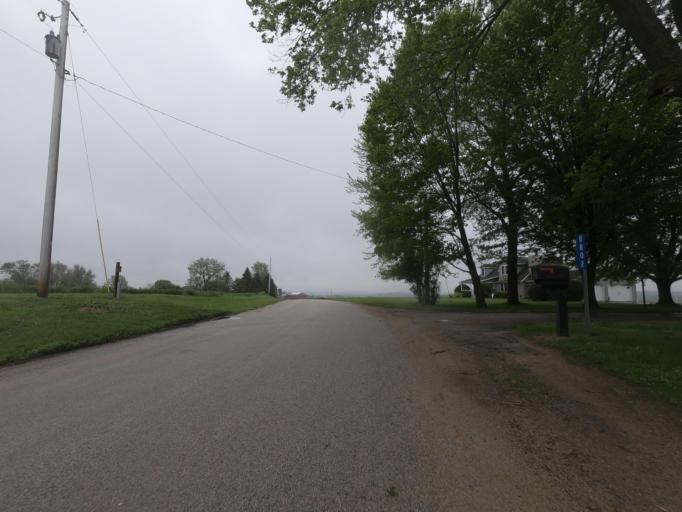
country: US
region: Wisconsin
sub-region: Grant County
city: Hazel Green
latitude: 42.5006
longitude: -90.5078
